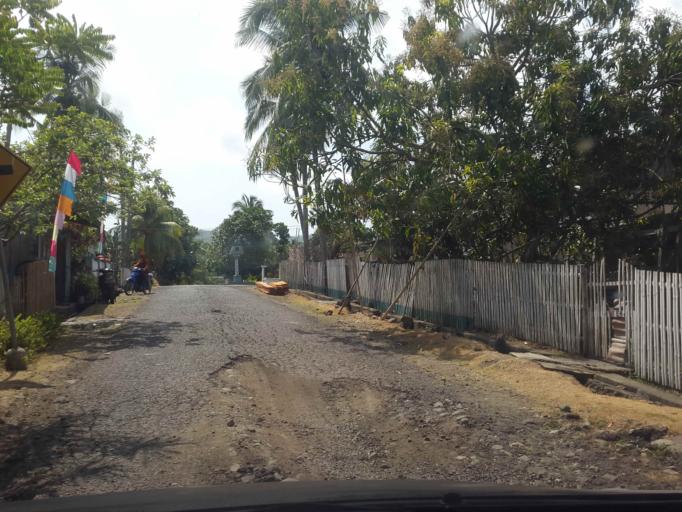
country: ID
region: South Sulawesi
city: Bantaeng
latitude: -6.2041
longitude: 120.4778
